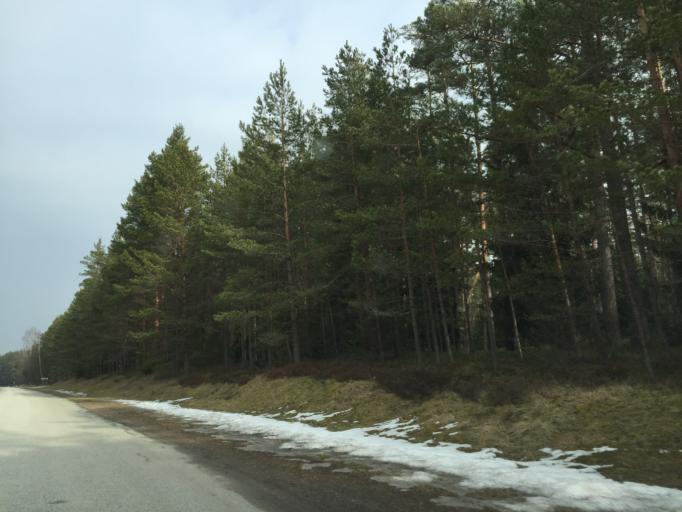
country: LV
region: Salacgrivas
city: Ainazi
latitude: 57.9635
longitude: 24.4059
